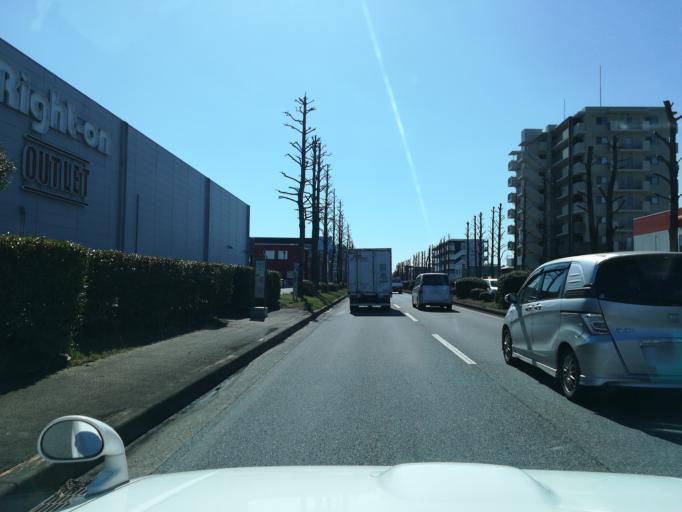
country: JP
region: Ibaraki
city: Naka
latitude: 36.0685
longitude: 140.1163
